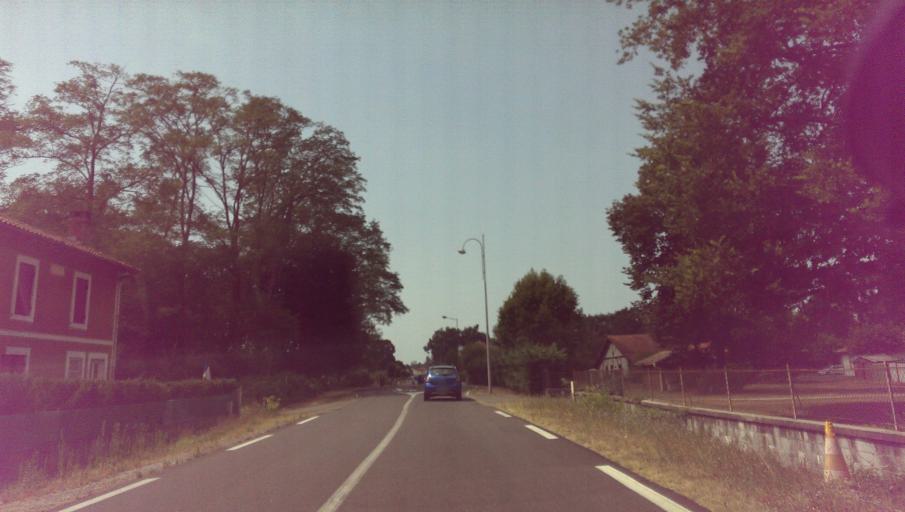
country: FR
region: Aquitaine
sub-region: Departement des Landes
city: Sabres
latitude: 44.1453
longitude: -0.7320
